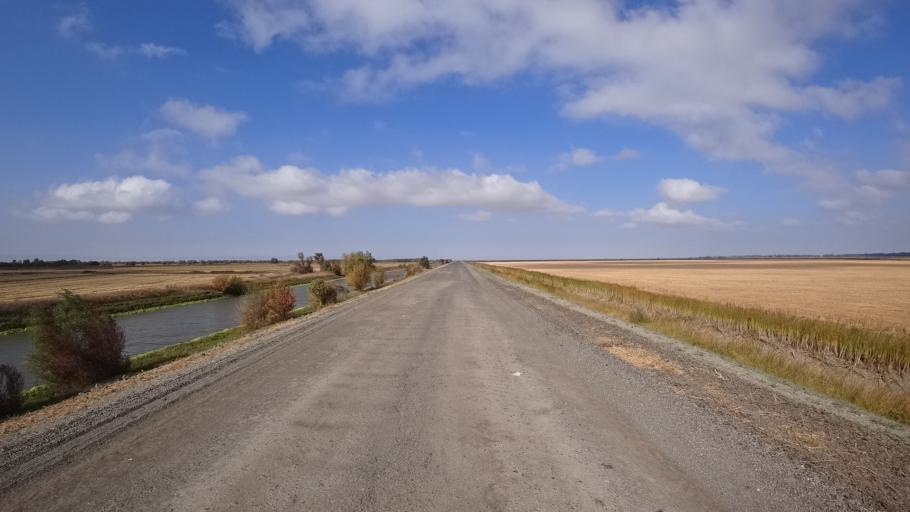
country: US
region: California
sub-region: Yolo County
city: Woodland
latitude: 38.8171
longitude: -121.7839
